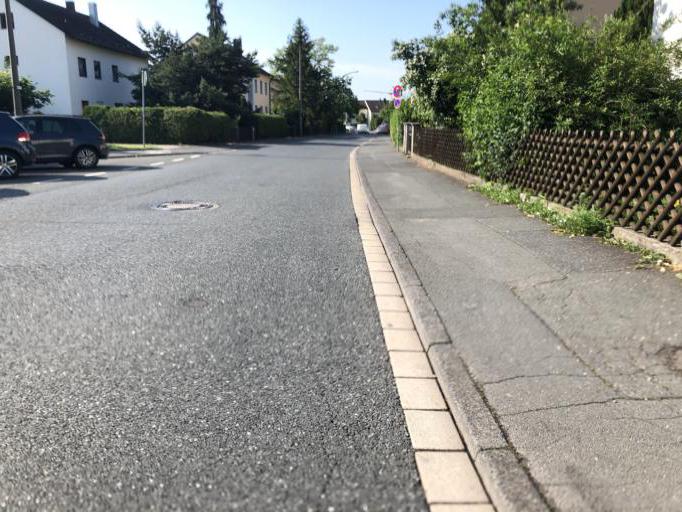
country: DE
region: Bavaria
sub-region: Regierungsbezirk Mittelfranken
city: Erlangen
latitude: 49.5756
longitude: 10.9931
